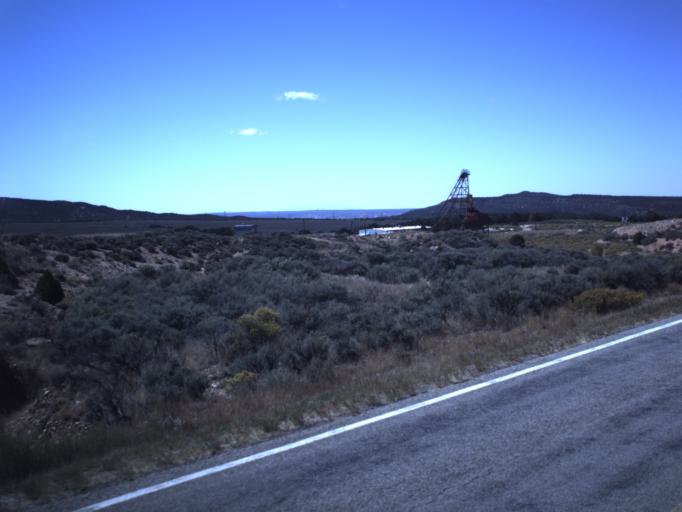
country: US
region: Utah
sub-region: Grand County
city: Moab
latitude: 38.3144
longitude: -109.3058
